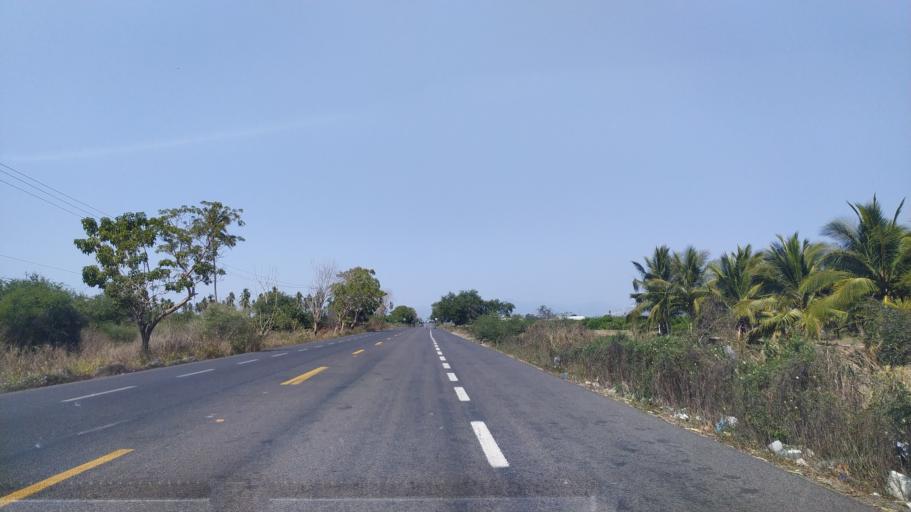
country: MX
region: Colima
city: Tecoman
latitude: 18.8404
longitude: -103.8223
